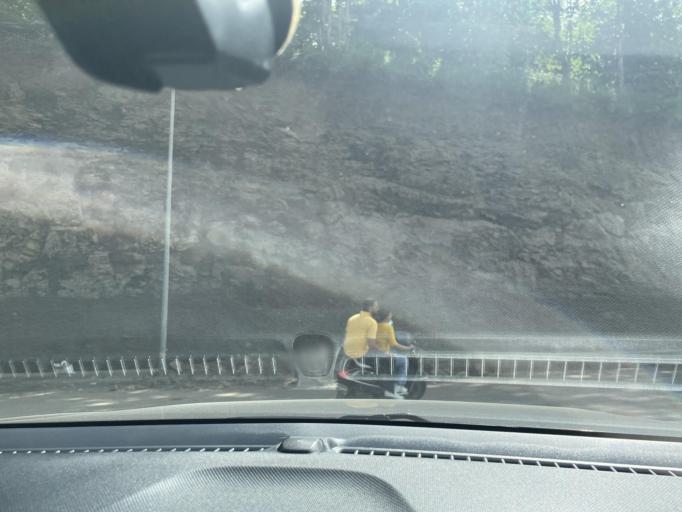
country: IN
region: Maharashtra
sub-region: Pune Division
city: Kharakvasla
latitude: 18.5049
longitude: 73.7866
